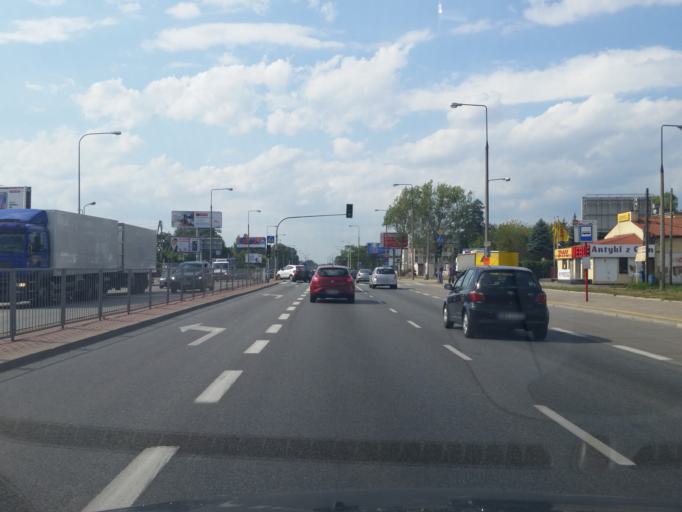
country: PL
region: Masovian Voivodeship
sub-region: Warszawa
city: Wlochy
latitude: 52.1919
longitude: 20.9496
